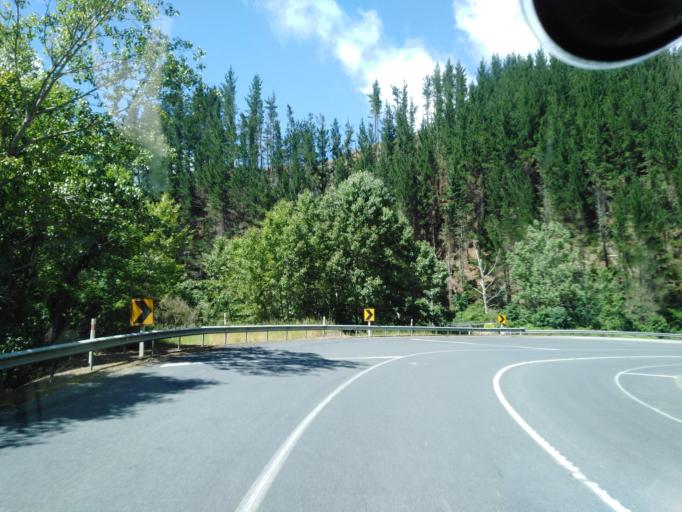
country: NZ
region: Nelson
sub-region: Nelson City
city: Nelson
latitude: -41.2291
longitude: 173.4016
